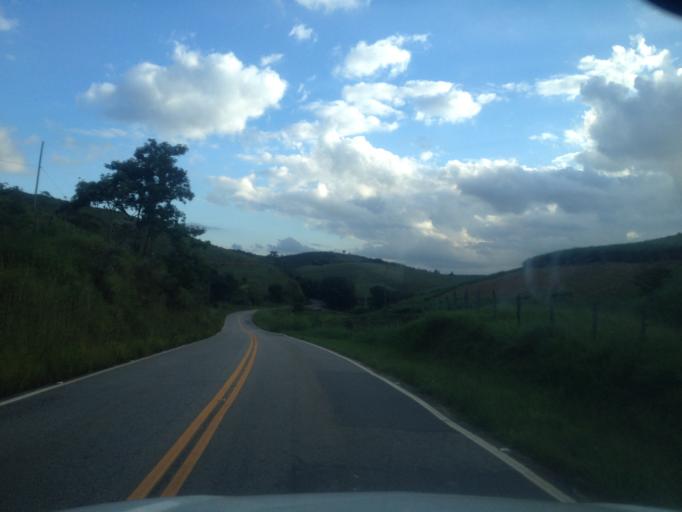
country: BR
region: Rio de Janeiro
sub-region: Quatis
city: Quatis
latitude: -22.3556
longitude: -44.2516
